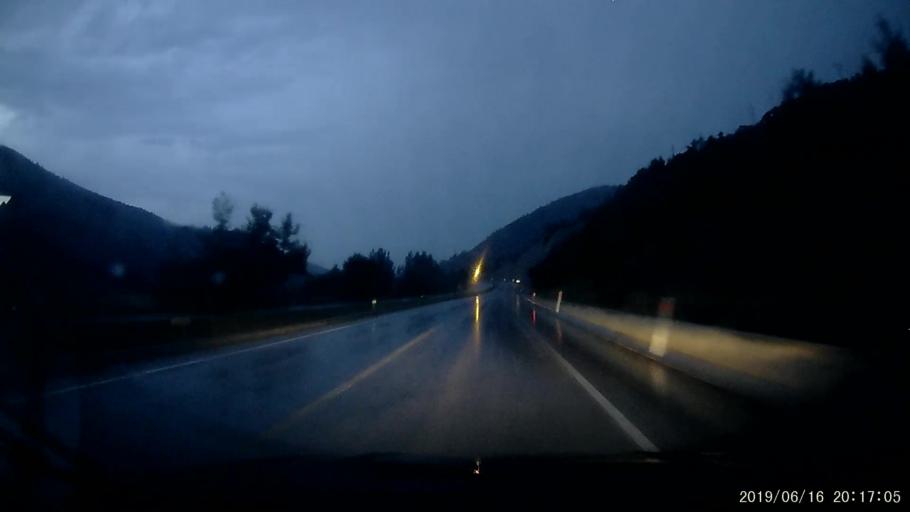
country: TR
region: Tokat
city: Resadiye
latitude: 40.3624
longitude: 37.4290
